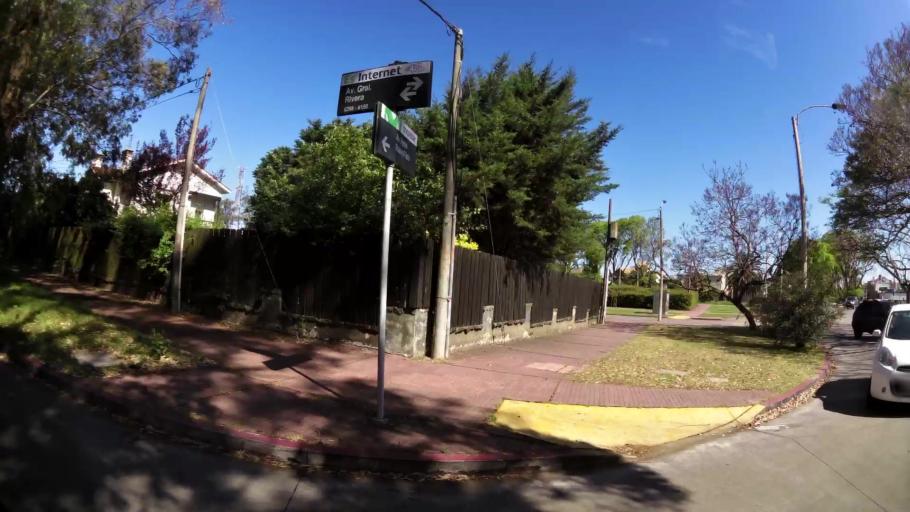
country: UY
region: Canelones
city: Paso de Carrasco
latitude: -34.8907
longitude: -56.0714
